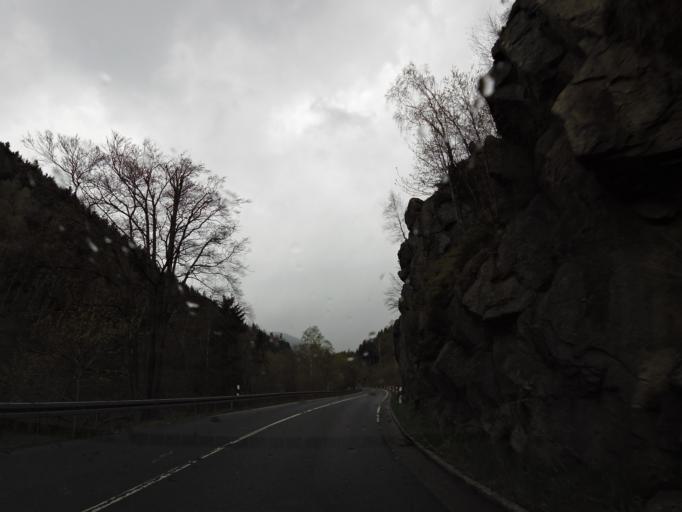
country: DE
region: Lower Saxony
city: Schulenberg im Oberharz
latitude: 51.8719
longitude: 10.4756
